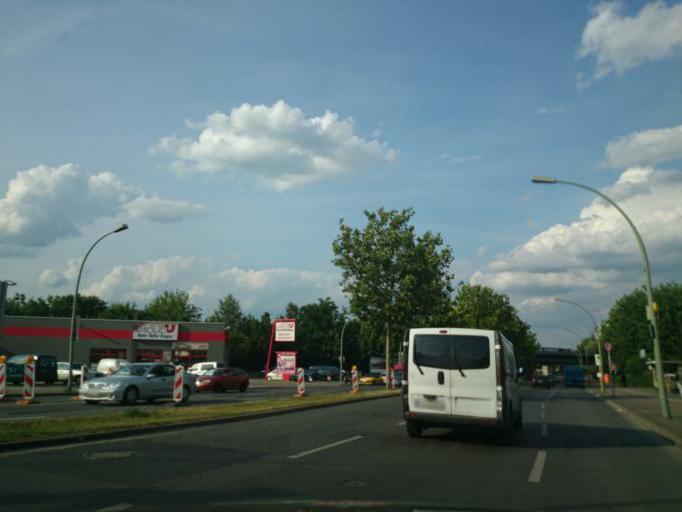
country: DE
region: Berlin
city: Plaenterwald
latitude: 52.4682
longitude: 13.4609
